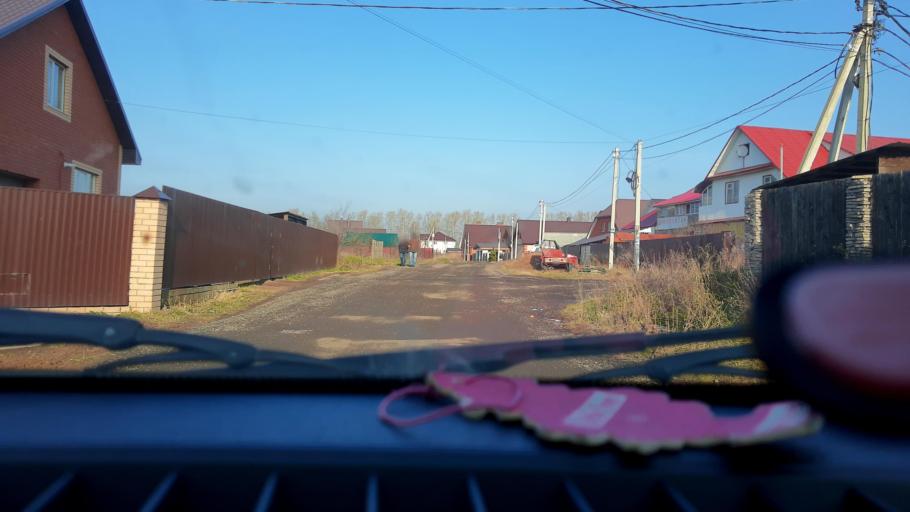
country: RU
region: Bashkortostan
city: Ufa
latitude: 54.6780
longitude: 56.0906
